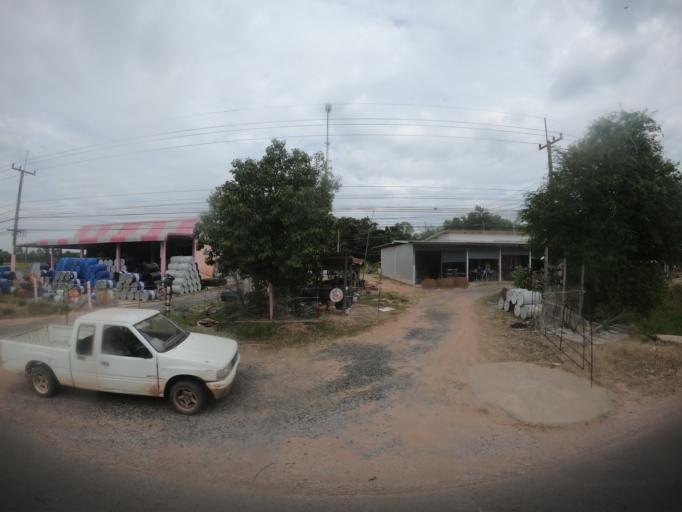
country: TH
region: Kalasin
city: Khong Chai
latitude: 16.1408
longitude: 103.4289
